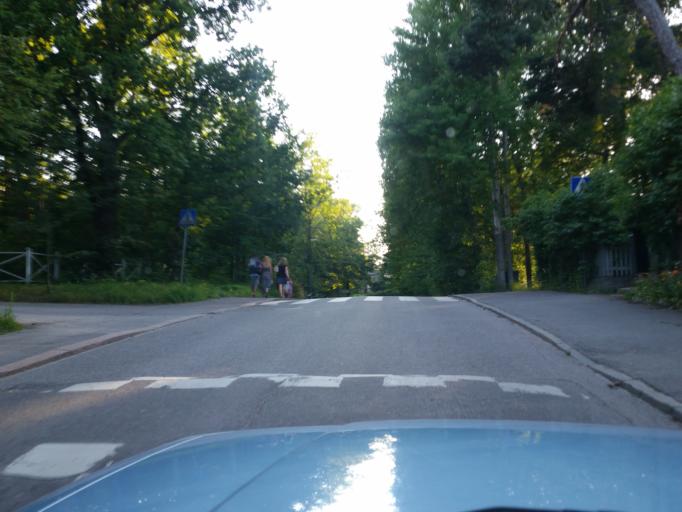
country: FI
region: Uusimaa
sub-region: Helsinki
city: Teekkarikylae
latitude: 60.1917
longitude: 24.8873
